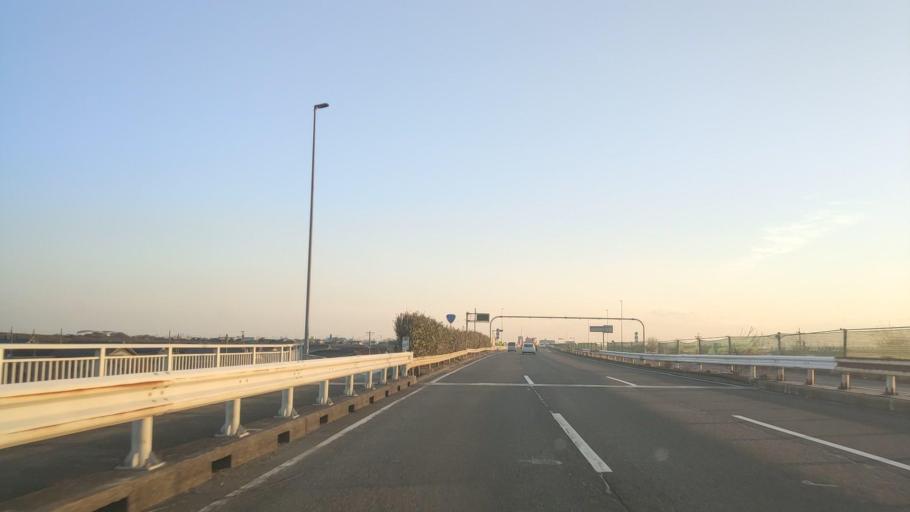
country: JP
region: Gifu
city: Kasamatsucho
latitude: 35.3741
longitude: 136.7842
